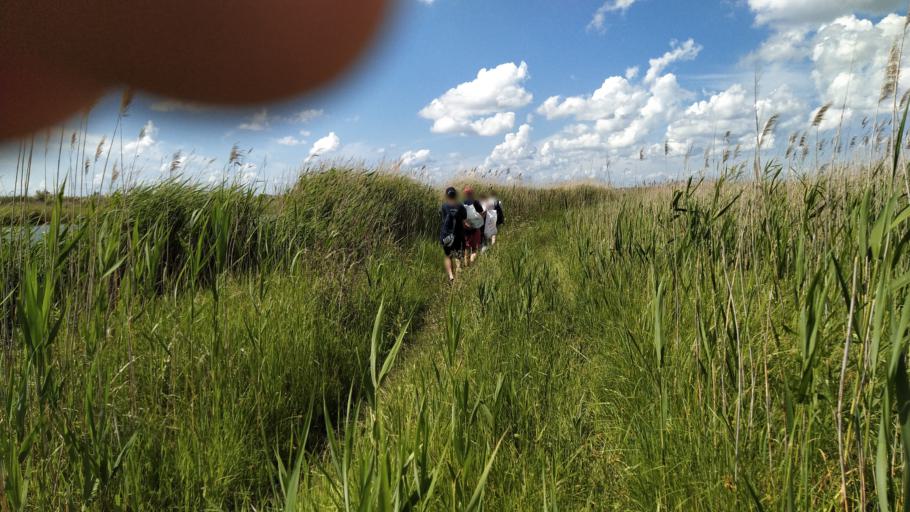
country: RU
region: Rostov
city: Bataysk
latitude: 47.1375
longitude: 39.6694
